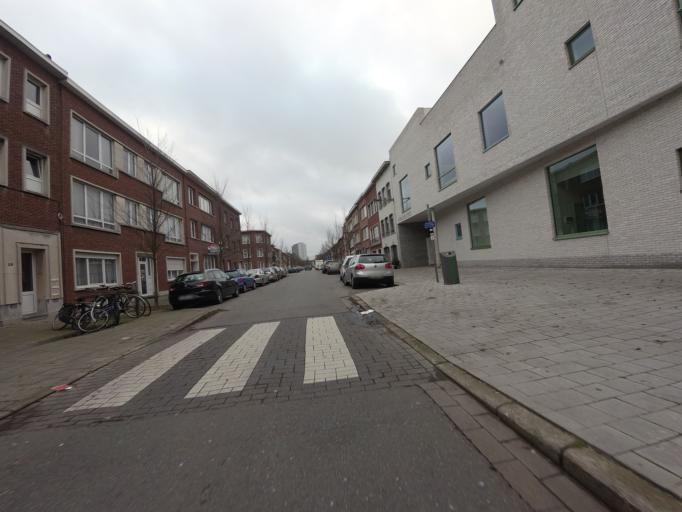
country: BE
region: Flanders
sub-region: Provincie Antwerpen
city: Hoboken
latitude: 51.1819
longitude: 4.3886
